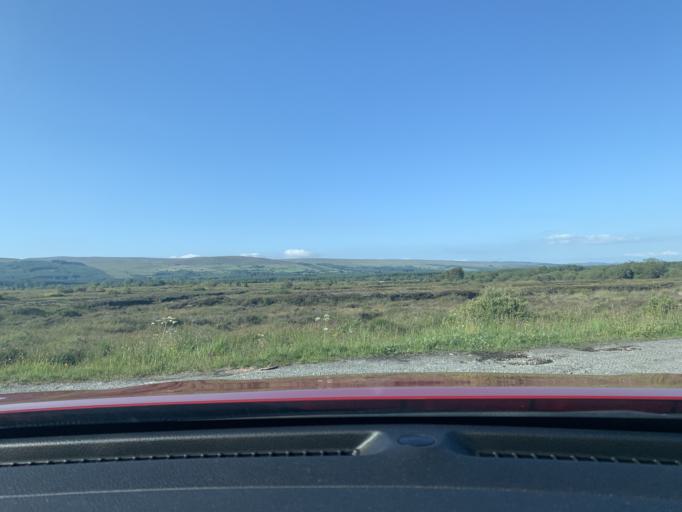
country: IE
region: Connaught
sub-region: Sligo
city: Tobercurry
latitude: 54.0702
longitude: -8.7996
